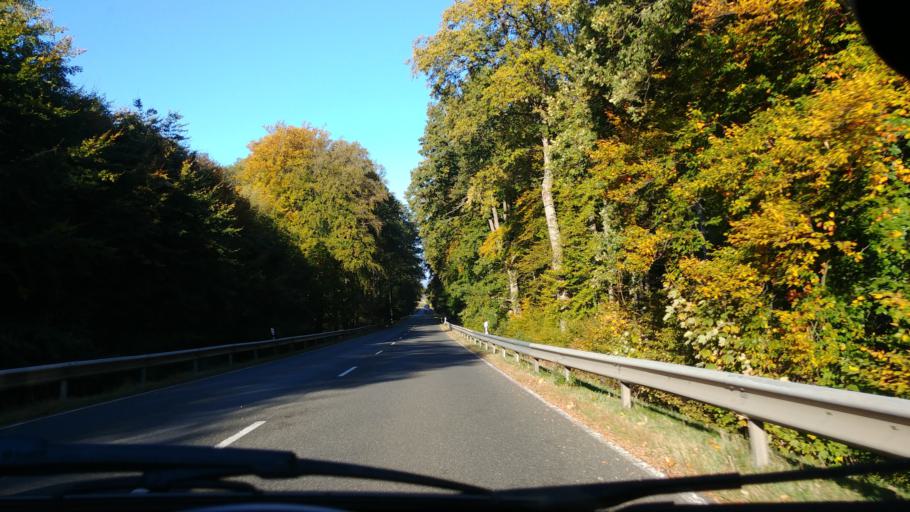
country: DE
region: Rheinland-Pfalz
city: Holzhausen an der Haide
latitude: 50.2091
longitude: 7.9306
